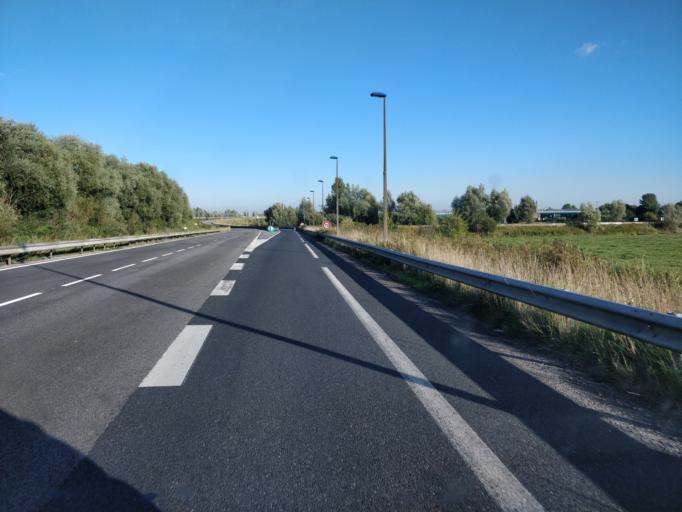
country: FR
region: Haute-Normandie
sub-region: Departement de la Seine-Maritime
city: Rogerville
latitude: 49.4940
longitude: 0.2590
